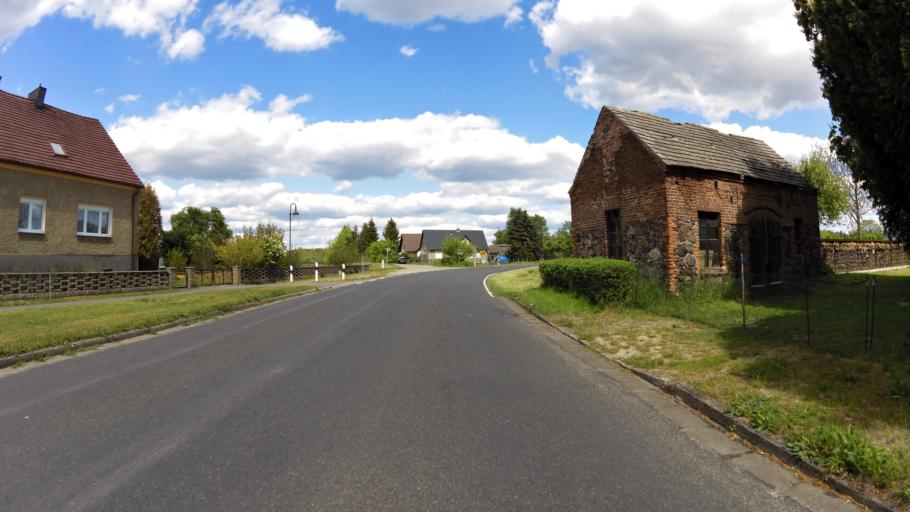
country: DE
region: Brandenburg
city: Diensdorf-Radlow
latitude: 52.1770
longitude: 14.0777
